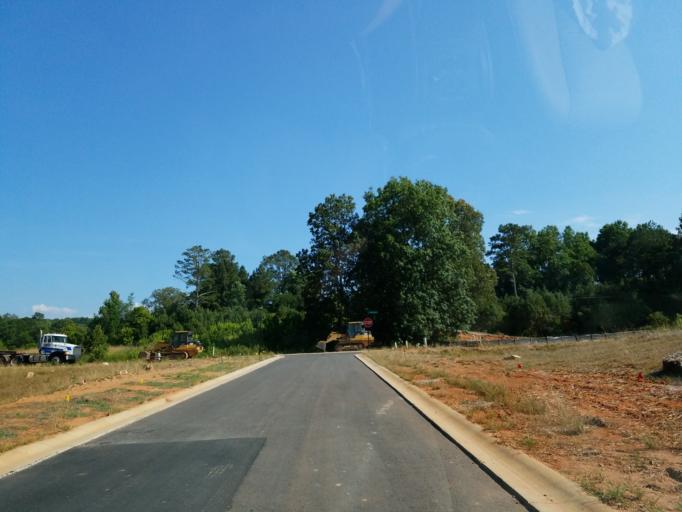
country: US
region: Georgia
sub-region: Fulton County
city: Milton
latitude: 34.1804
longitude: -84.3294
